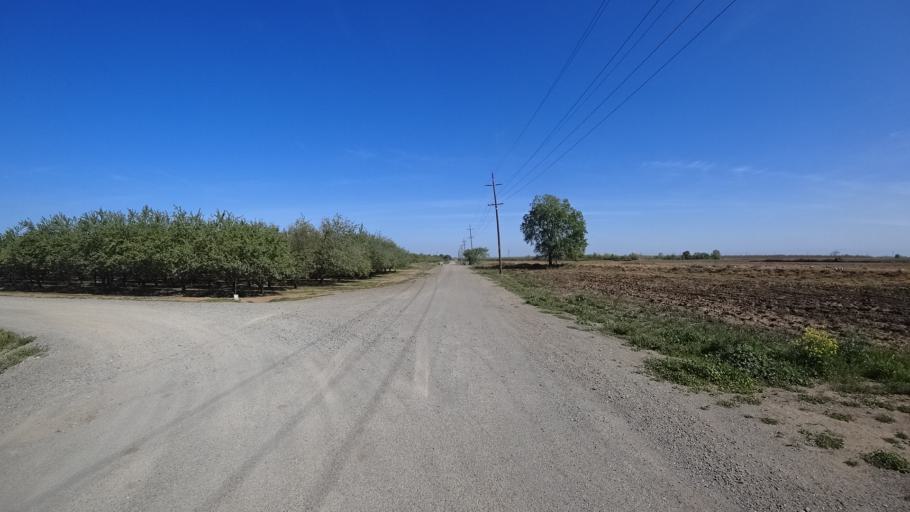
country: US
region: California
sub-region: Glenn County
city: Willows
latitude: 39.5479
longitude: -122.1861
